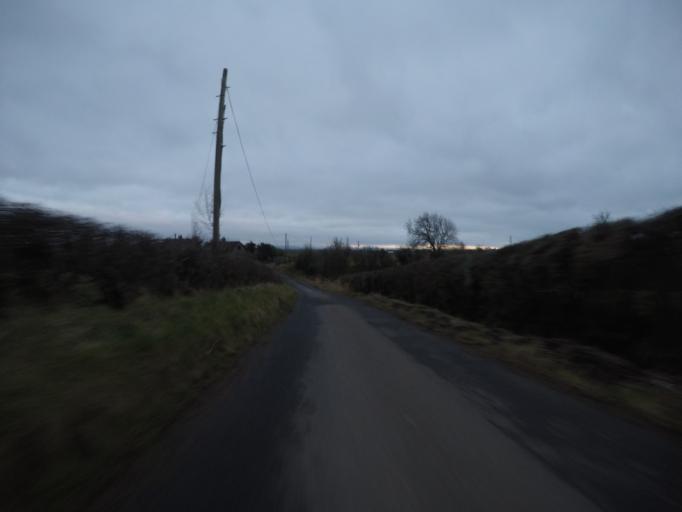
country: GB
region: Scotland
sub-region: North Ayrshire
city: Kilwinning
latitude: 55.6759
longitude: -4.7238
